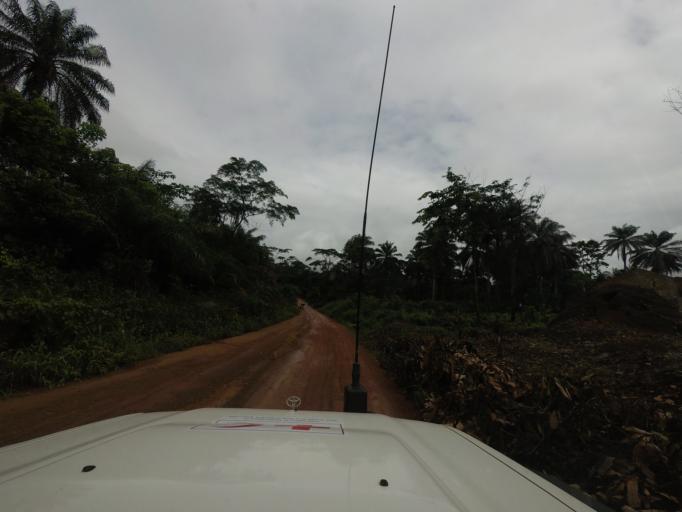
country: GN
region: Nzerekore
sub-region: Nzerekore Prefecture
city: Nzerekore
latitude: 7.7300
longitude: -8.8530
